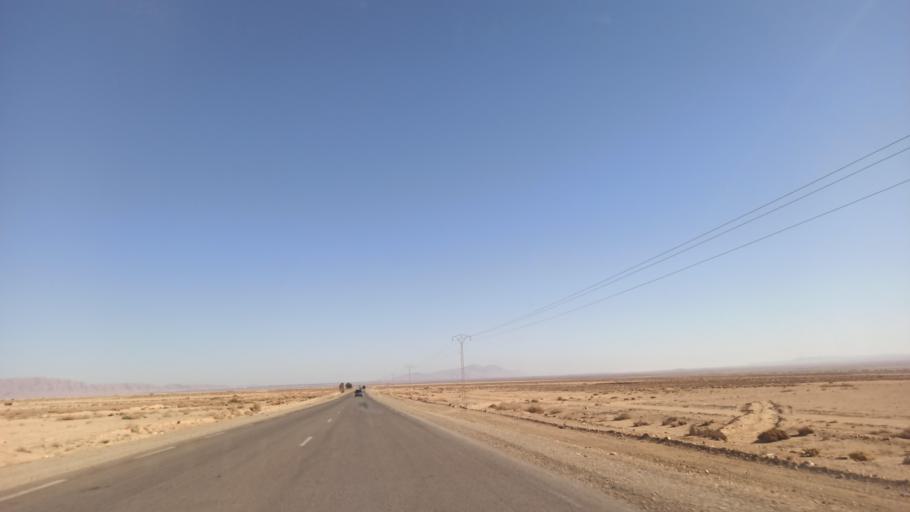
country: TN
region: Gafsa
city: Al Metlaoui
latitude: 34.3195
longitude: 8.5153
